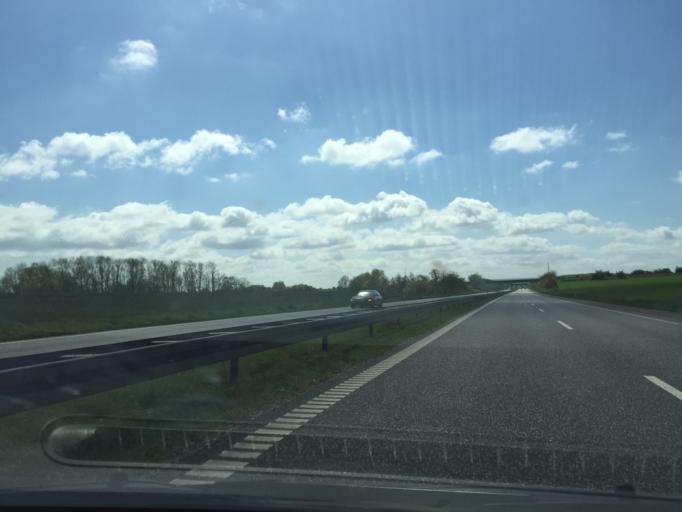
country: DK
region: Zealand
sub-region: Guldborgsund Kommune
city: Norre Alslev
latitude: 54.8738
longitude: 11.8908
